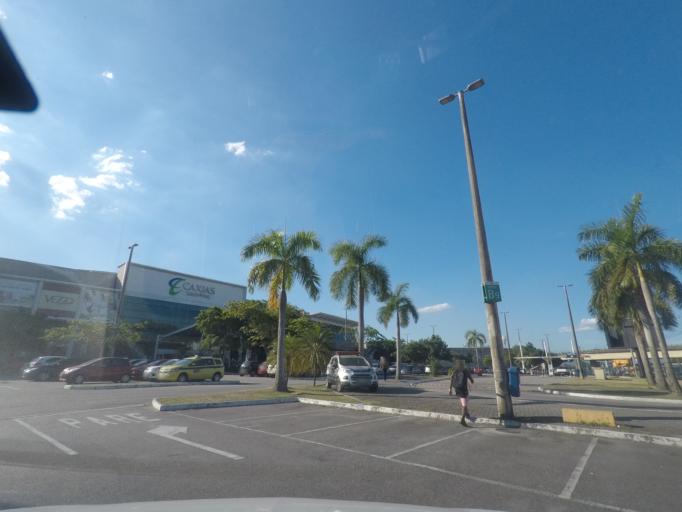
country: BR
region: Rio de Janeiro
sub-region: Duque De Caxias
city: Duque de Caxias
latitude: -22.7876
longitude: -43.2858
